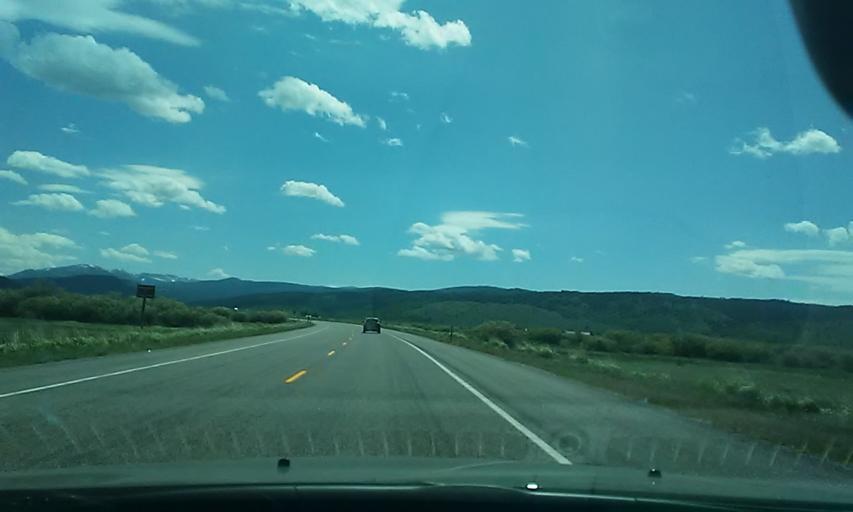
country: US
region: Wyoming
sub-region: Teton County
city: Jackson
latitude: 43.8330
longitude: -110.4250
